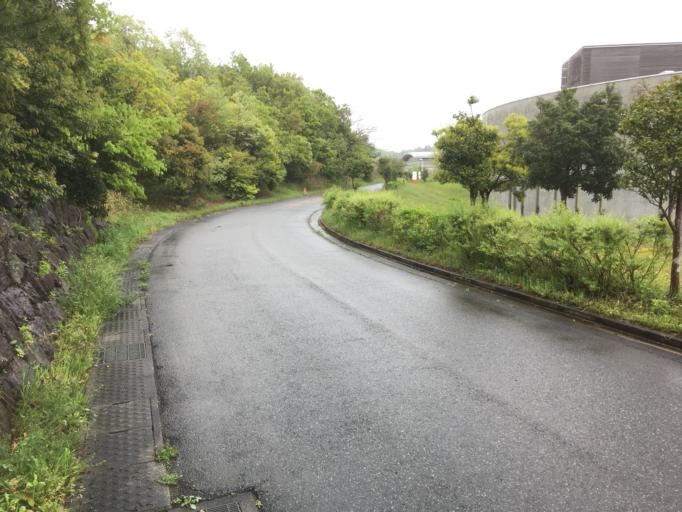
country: JP
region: Tottori
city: Tottori
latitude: 35.4519
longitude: 134.2555
